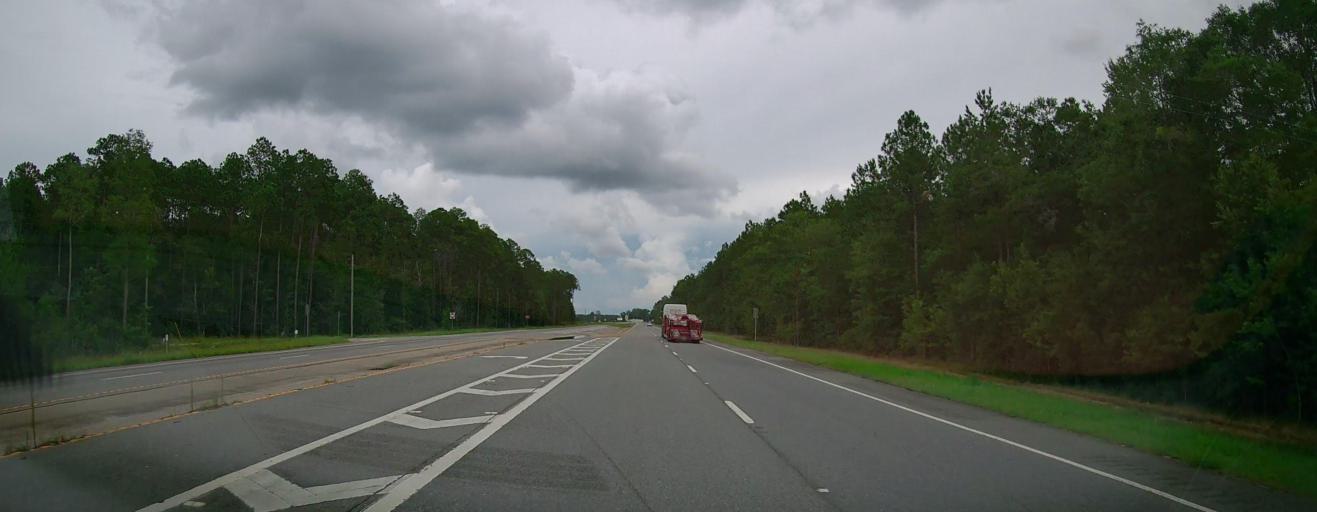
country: US
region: Georgia
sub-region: Wayne County
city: Jesup
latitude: 31.6711
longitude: -82.0584
